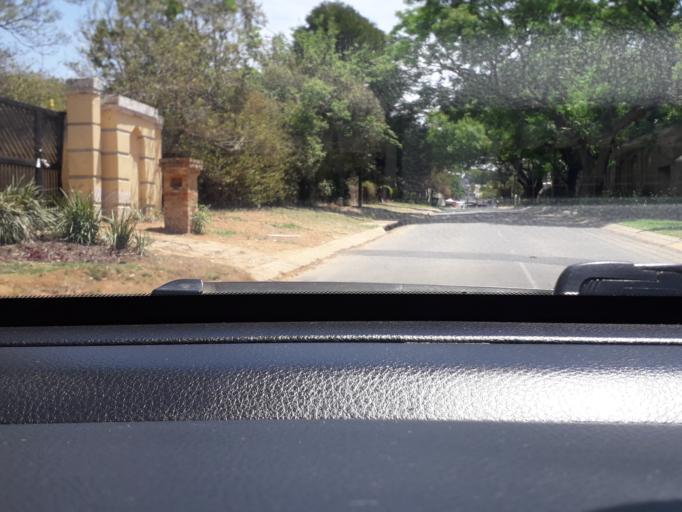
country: ZA
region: Gauteng
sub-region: City of Johannesburg Metropolitan Municipality
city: Modderfontein
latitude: -26.0990
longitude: 28.0725
